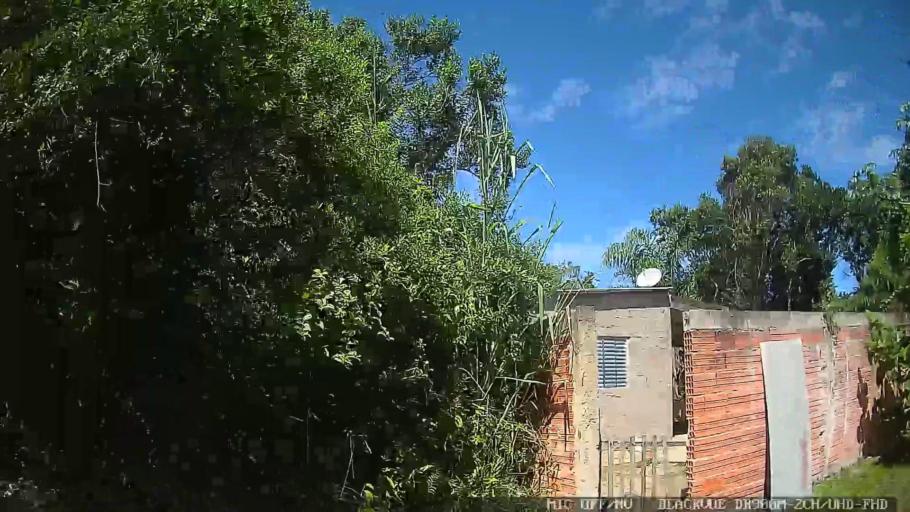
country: BR
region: Sao Paulo
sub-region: Itanhaem
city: Itanhaem
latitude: -24.2311
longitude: -46.8950
